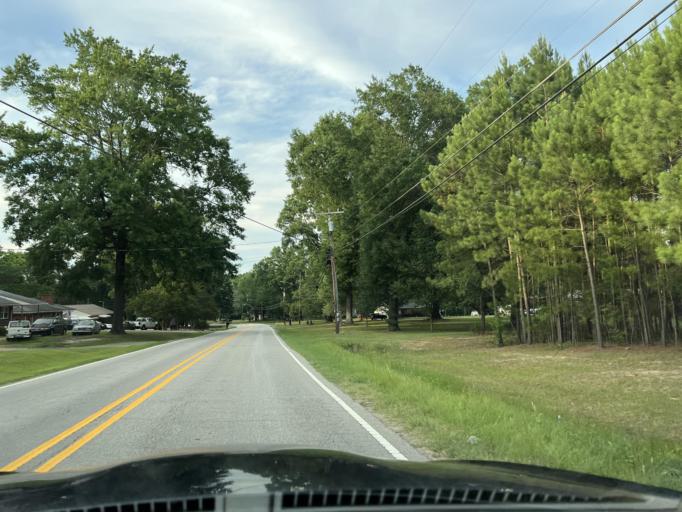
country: US
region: North Carolina
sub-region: Durham County
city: Durham
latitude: 35.9772
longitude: -78.8420
